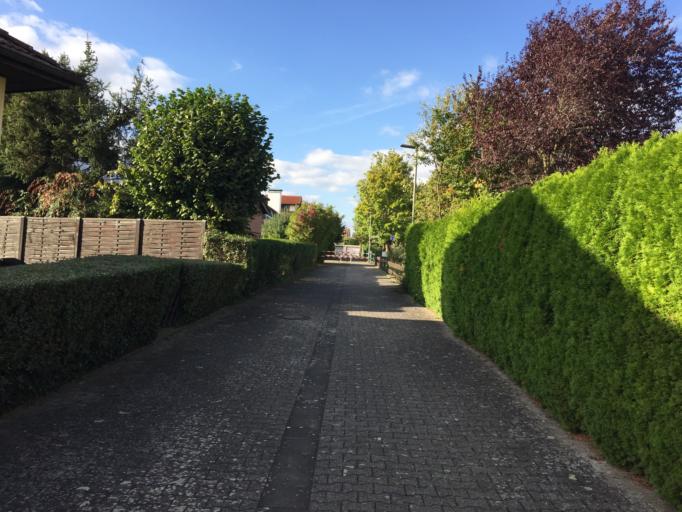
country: DE
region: Hesse
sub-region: Regierungsbezirk Darmstadt
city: Rockenberg
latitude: 50.4622
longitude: 8.7364
